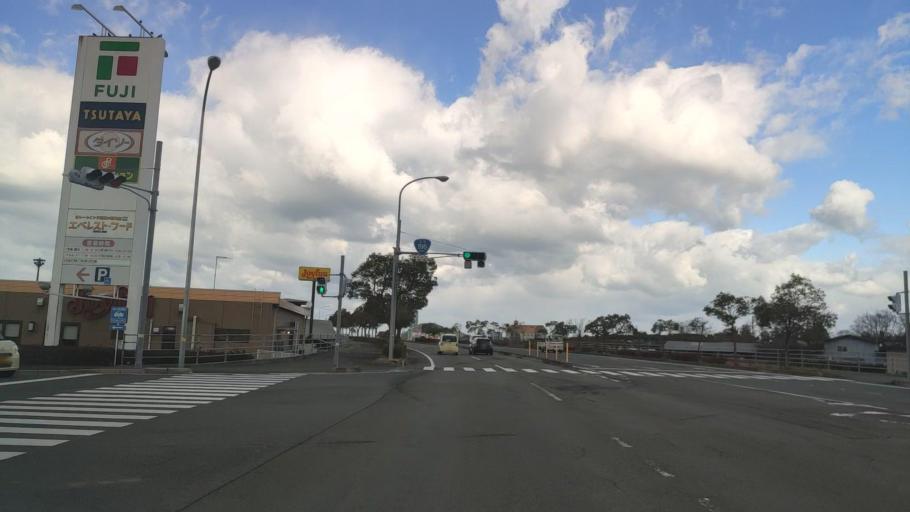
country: JP
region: Ehime
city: Hojo
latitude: 33.9457
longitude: 132.7760
